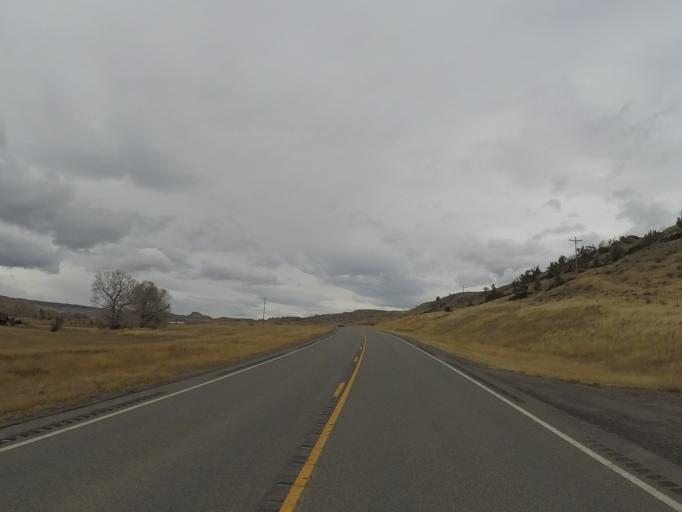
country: US
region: Montana
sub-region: Sweet Grass County
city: Big Timber
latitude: 45.9134
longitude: -109.9781
